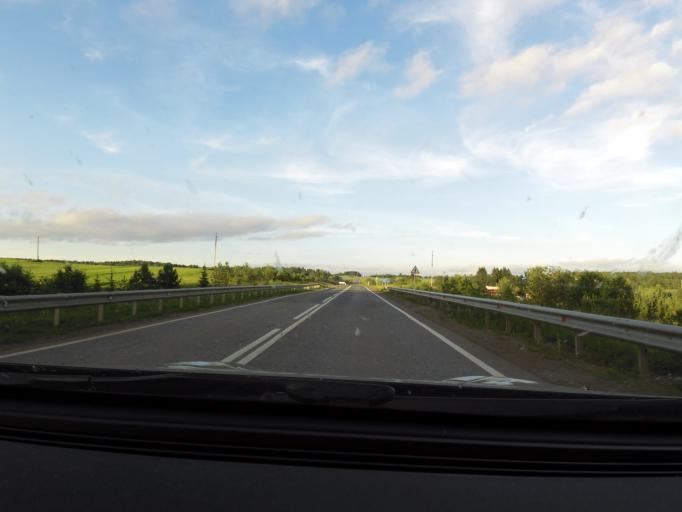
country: RU
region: Perm
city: Siva
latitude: 58.4863
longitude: 54.0894
